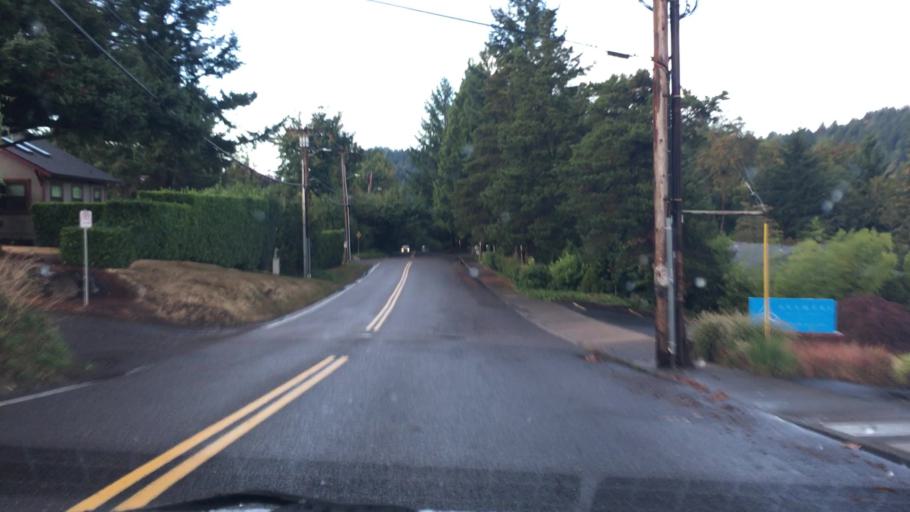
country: US
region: Oregon
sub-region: Washington County
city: Garden Home-Whitford
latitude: 45.4767
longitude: -122.7077
